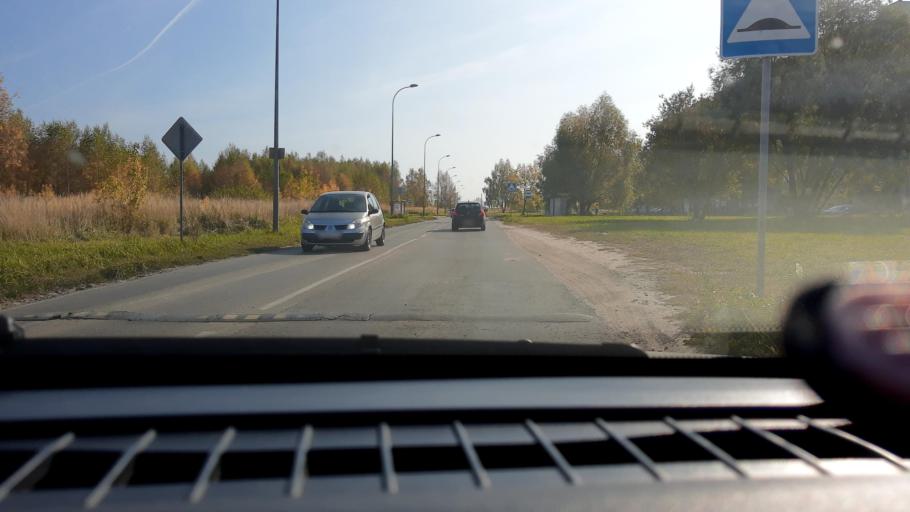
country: RU
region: Nizjnij Novgorod
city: Kstovo
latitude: 56.1528
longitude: 44.2190
